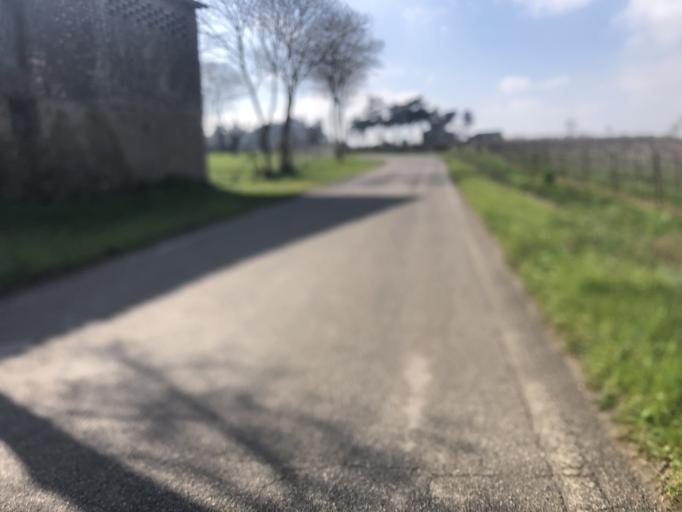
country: IT
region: Veneto
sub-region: Provincia di Verona
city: San Giorgio in Salici
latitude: 45.3860
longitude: 10.7970
